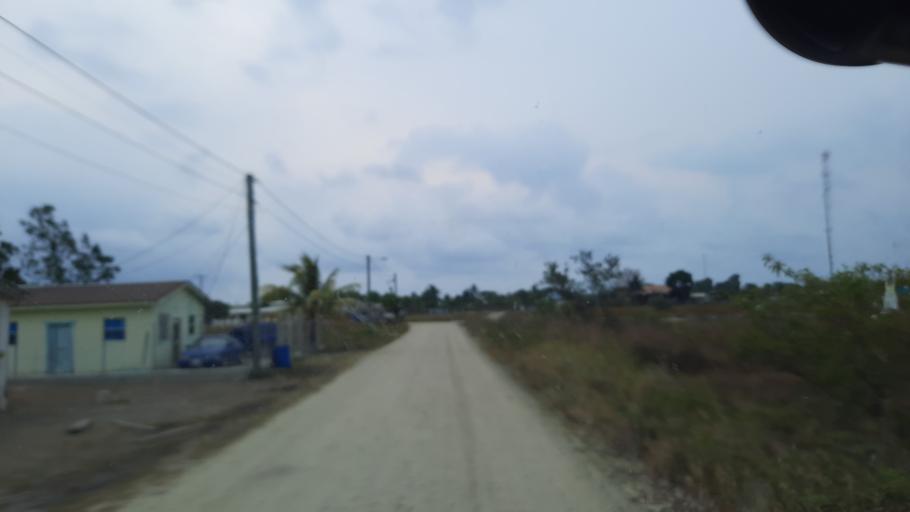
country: BZ
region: Stann Creek
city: Placencia
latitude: 16.5327
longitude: -88.4249
